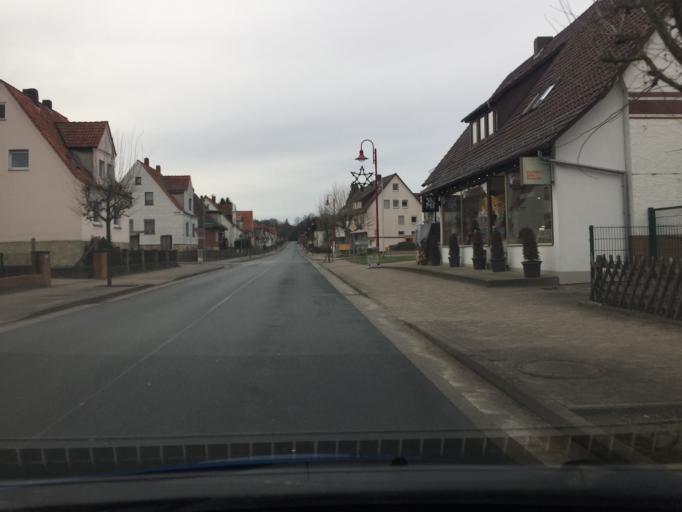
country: DE
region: Lower Saxony
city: Duingen
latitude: 52.0038
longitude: 9.6941
